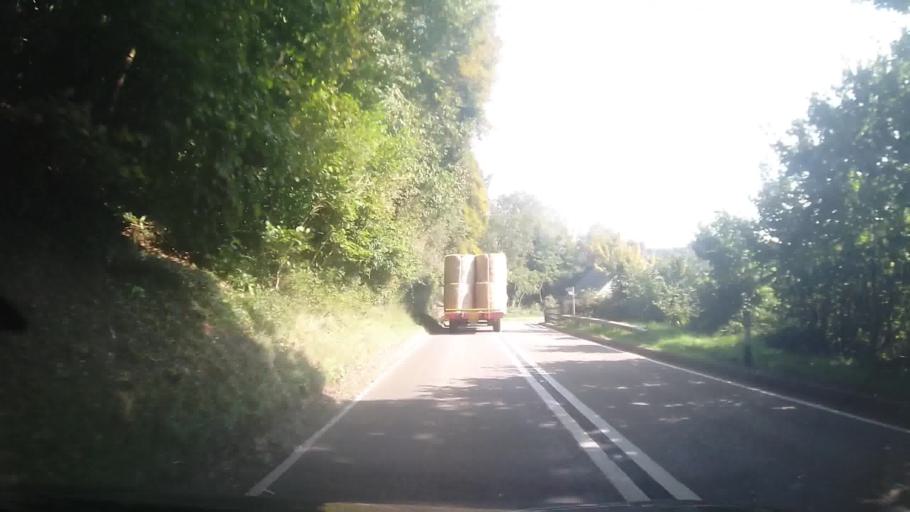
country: GB
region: Wales
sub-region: Pembrokeshire
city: Nevern
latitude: 52.0168
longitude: -4.7647
